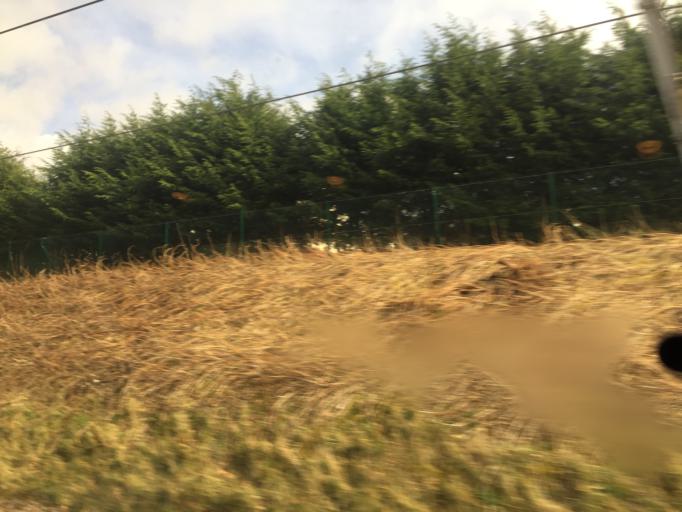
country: GB
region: Scotland
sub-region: South Lanarkshire
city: Douglas
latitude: 55.4899
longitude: -3.6872
